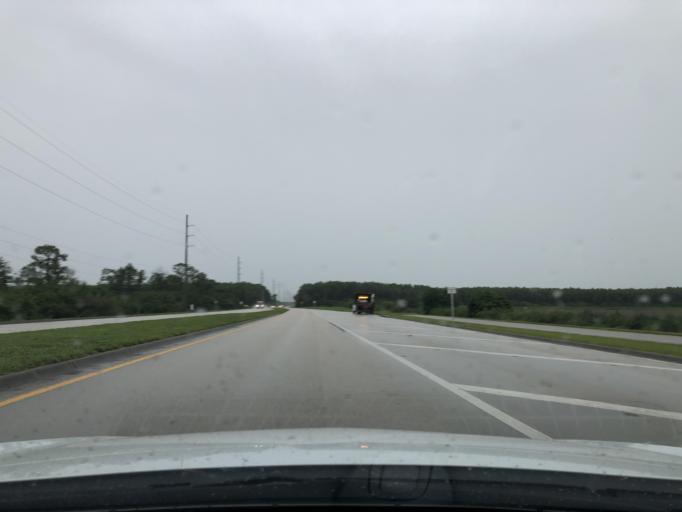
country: US
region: Florida
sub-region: Collier County
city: Orangetree
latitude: 26.2942
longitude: -81.4860
